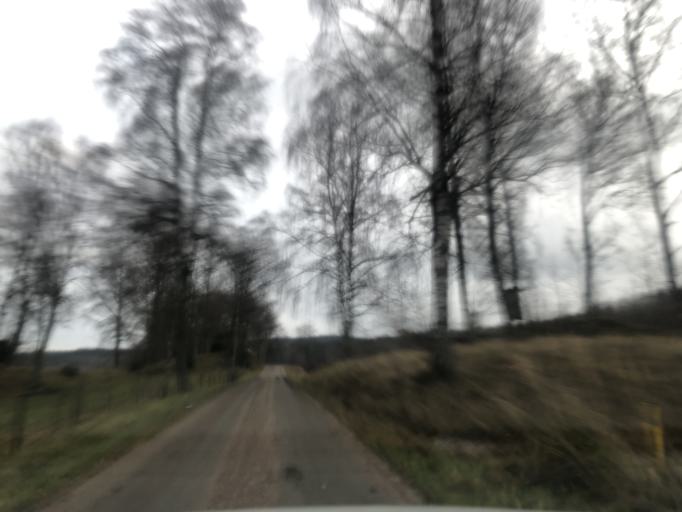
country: SE
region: Vaestra Goetaland
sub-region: Ulricehamns Kommun
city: Ulricehamn
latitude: 57.9051
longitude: 13.4858
